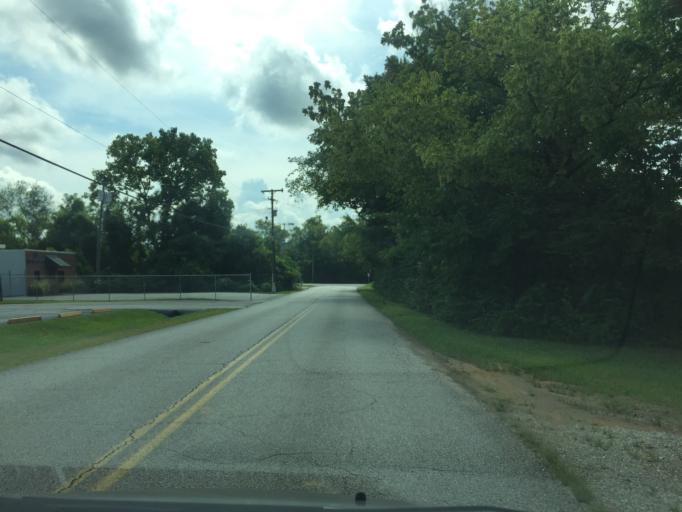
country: US
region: Tennessee
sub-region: Hamilton County
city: East Chattanooga
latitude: 35.0691
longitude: -85.2644
